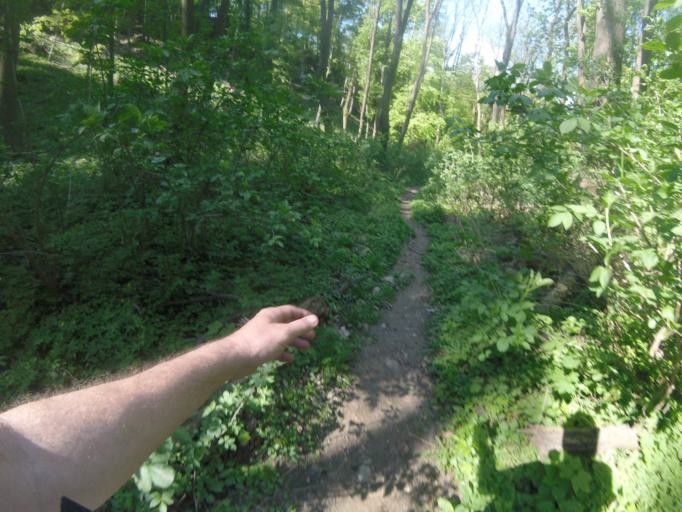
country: HU
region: Komarom-Esztergom
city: Piliscsev
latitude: 47.7066
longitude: 18.8490
